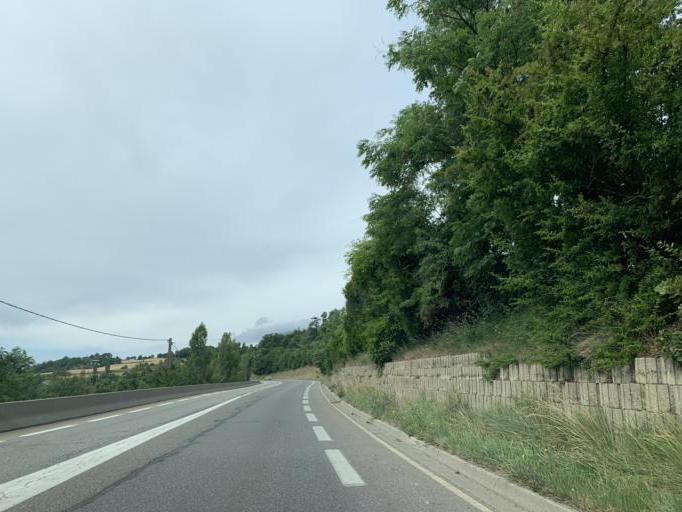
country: FR
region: Provence-Alpes-Cote d'Azur
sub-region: Departement des Hautes-Alpes
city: Gap
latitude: 44.5555
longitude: 6.0428
